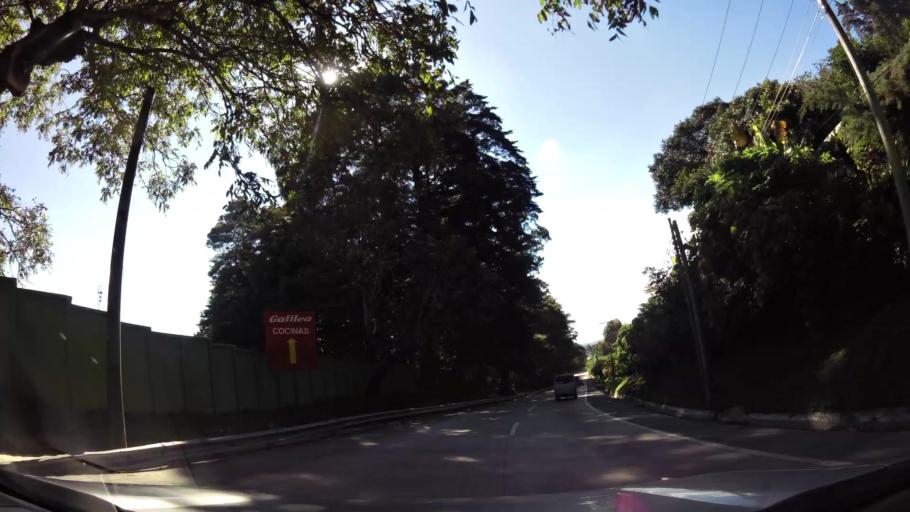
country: GT
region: Sacatepequez
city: Santa Lucia Milpas Altas
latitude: 14.5788
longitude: -90.6672
